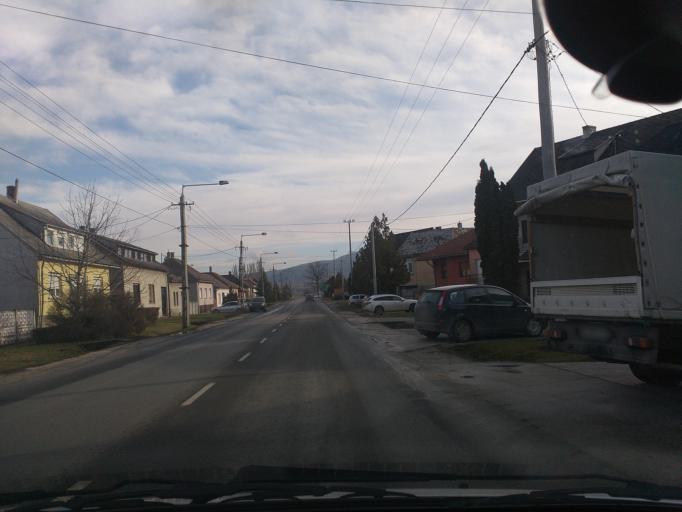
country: HU
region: Komarom-Esztergom
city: Tat
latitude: 47.7422
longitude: 18.6492
